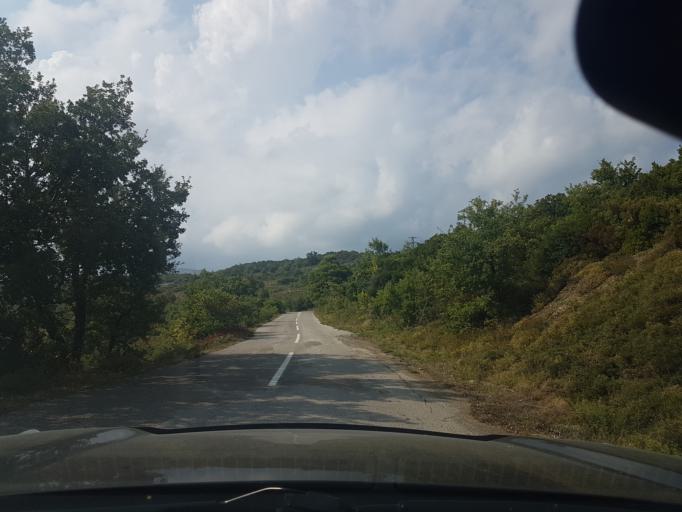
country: GR
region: Central Greece
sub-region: Nomos Evvoias
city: Yimnon
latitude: 38.5387
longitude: 23.9688
